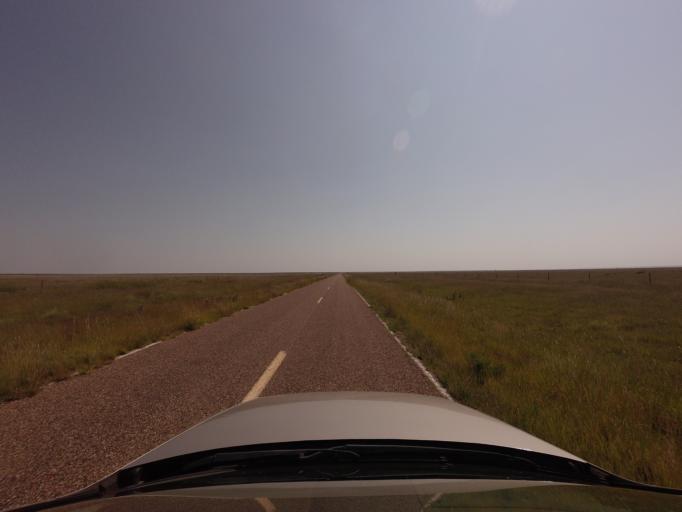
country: US
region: New Mexico
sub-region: Curry County
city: Cannon Air Force Base
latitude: 34.6333
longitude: -103.4294
